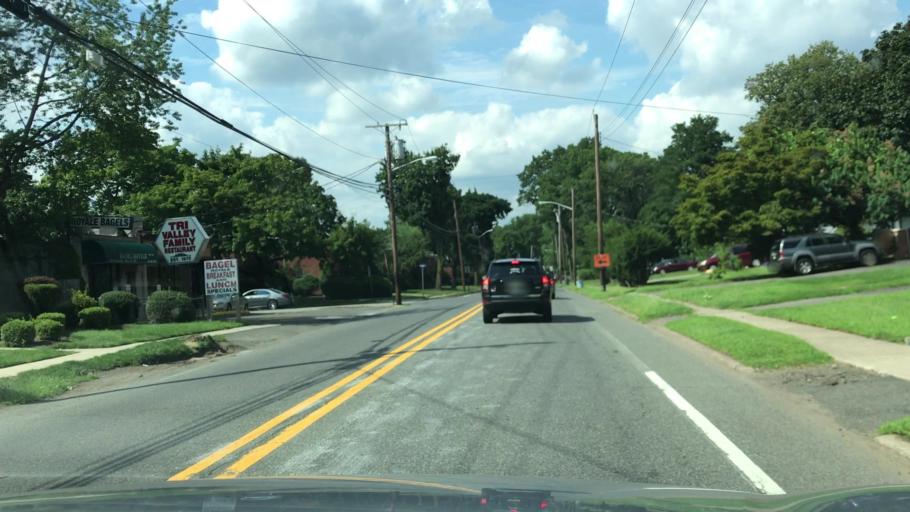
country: US
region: New Jersey
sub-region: Bergen County
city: Demarest
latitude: 40.9516
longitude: -73.9758
